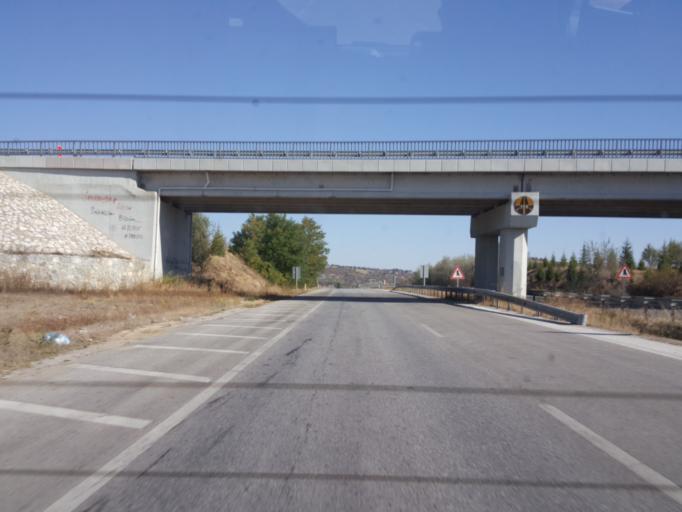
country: TR
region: Corum
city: Alaca
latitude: 40.2933
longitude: 34.6525
